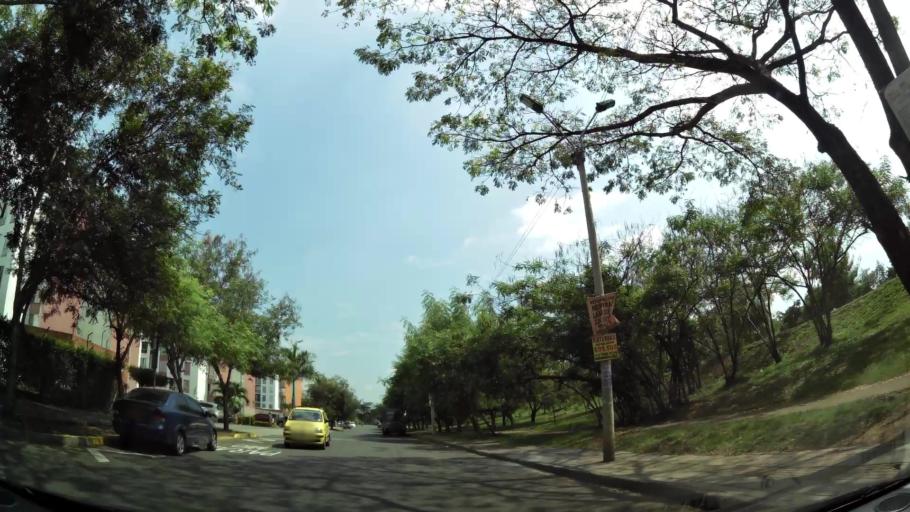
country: CO
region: Valle del Cauca
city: Cali
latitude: 3.4955
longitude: -76.4991
